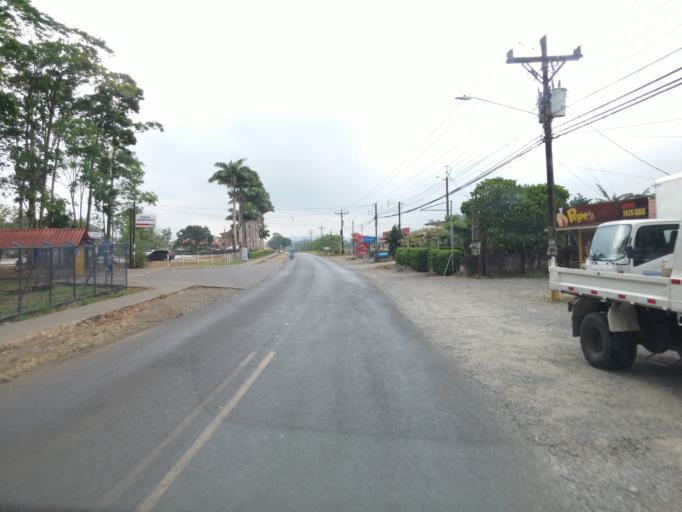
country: CR
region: Alajuela
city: Quesada
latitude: 10.3597
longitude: -84.5094
